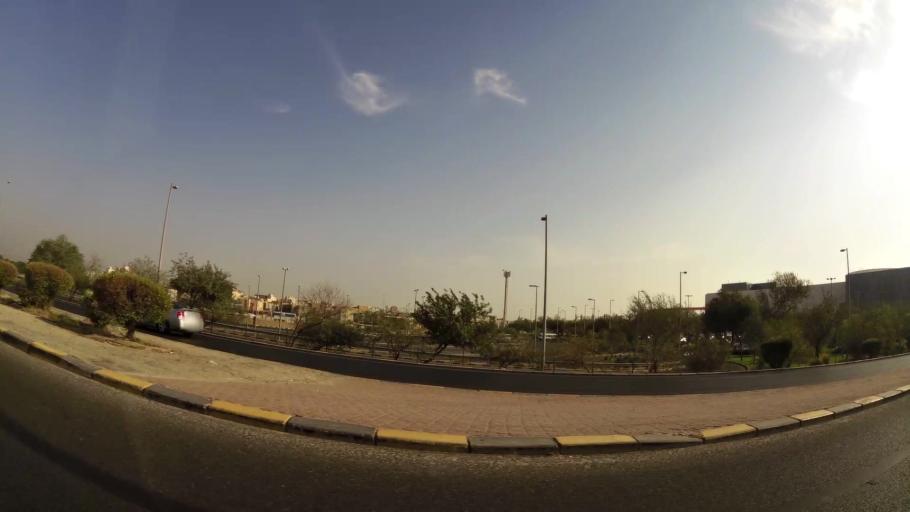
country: KW
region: Al Farwaniyah
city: Janub as Surrah
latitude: 29.2676
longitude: 47.9893
